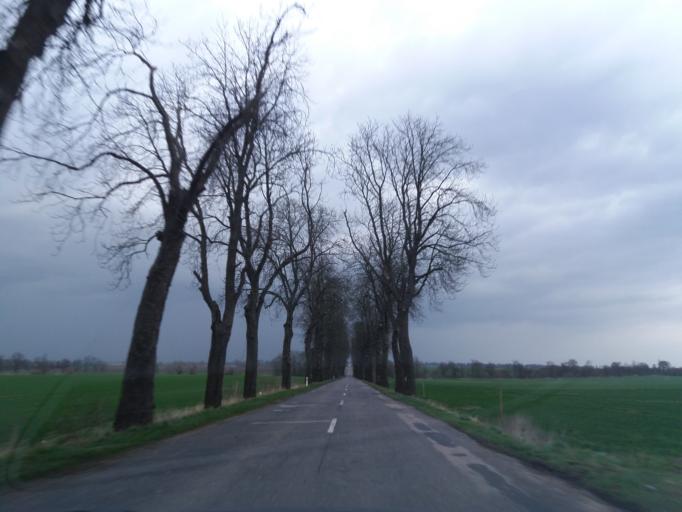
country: PL
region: West Pomeranian Voivodeship
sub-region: Powiat pyrzycki
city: Przelewice
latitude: 53.1695
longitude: 15.0621
